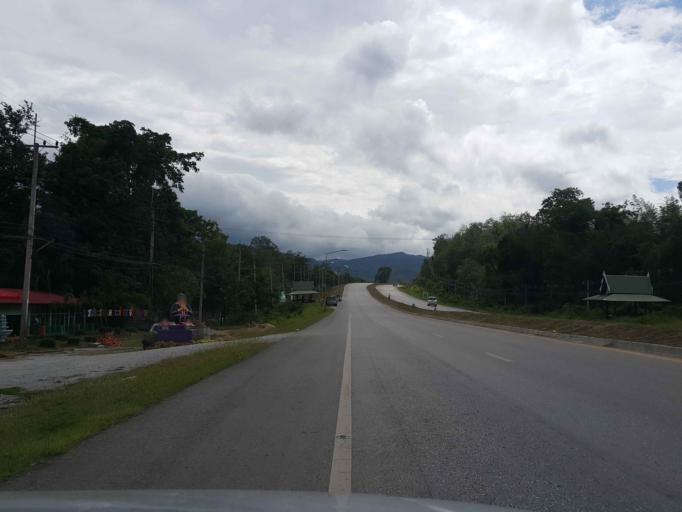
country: TH
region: Tak
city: Tak
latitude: 16.8070
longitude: 99.0544
